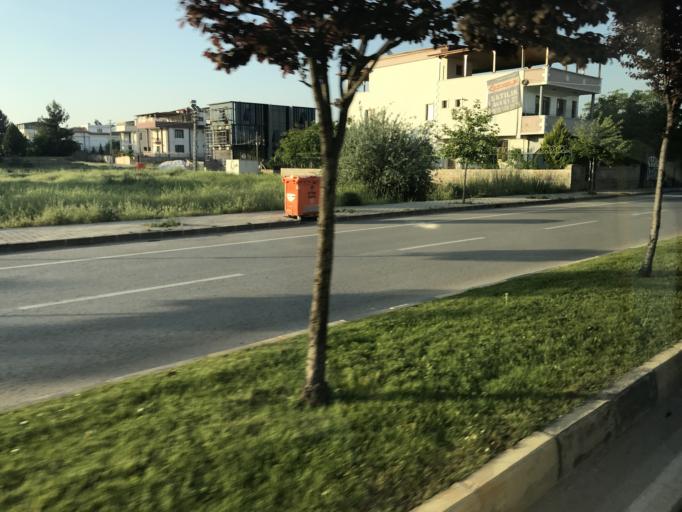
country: TR
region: Gaziantep
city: Sahinbey
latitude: 37.0545
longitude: 37.3235
